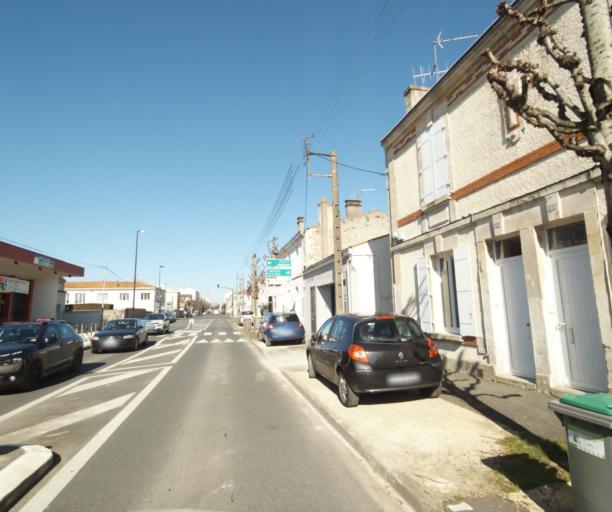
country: FR
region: Poitou-Charentes
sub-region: Departement des Deux-Sevres
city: Niort
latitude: 46.3127
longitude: -0.4656
